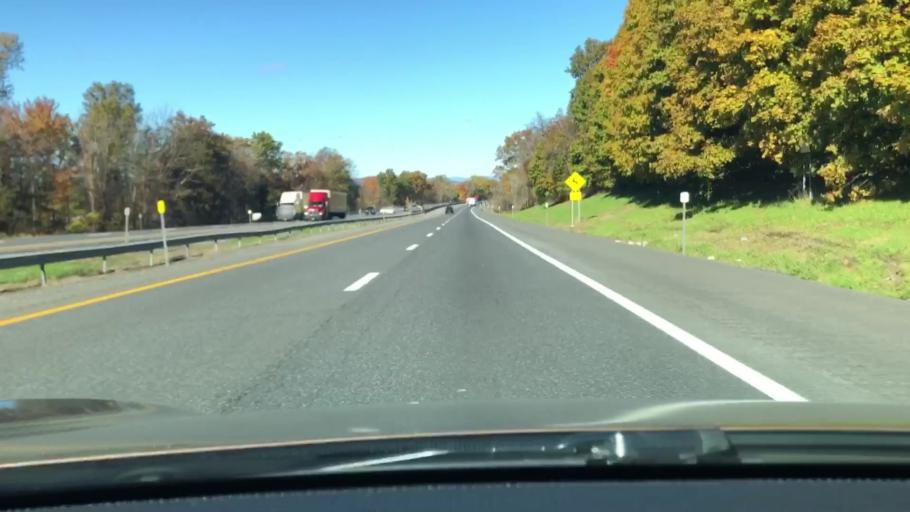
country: US
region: New York
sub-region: Ulster County
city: Clintondale
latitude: 41.6710
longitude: -74.0794
